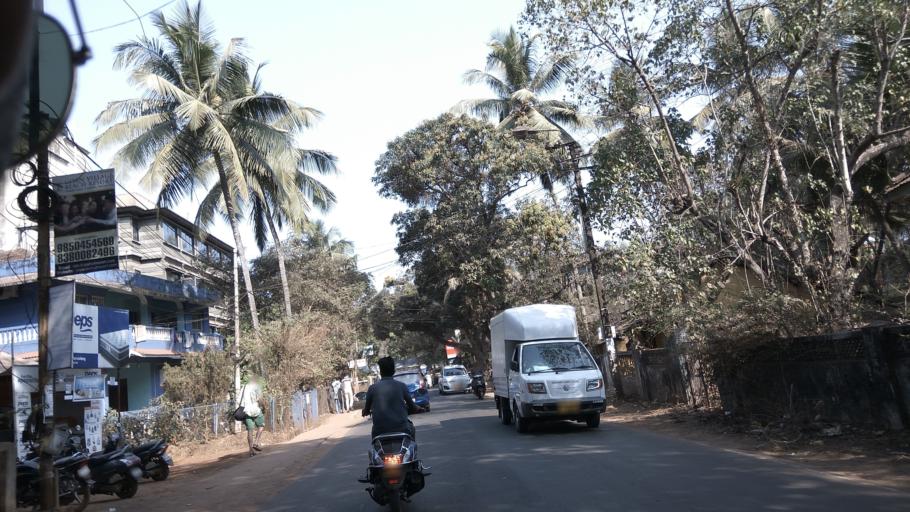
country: IN
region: Goa
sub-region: North Goa
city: Candolim
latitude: 15.5250
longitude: 73.7662
